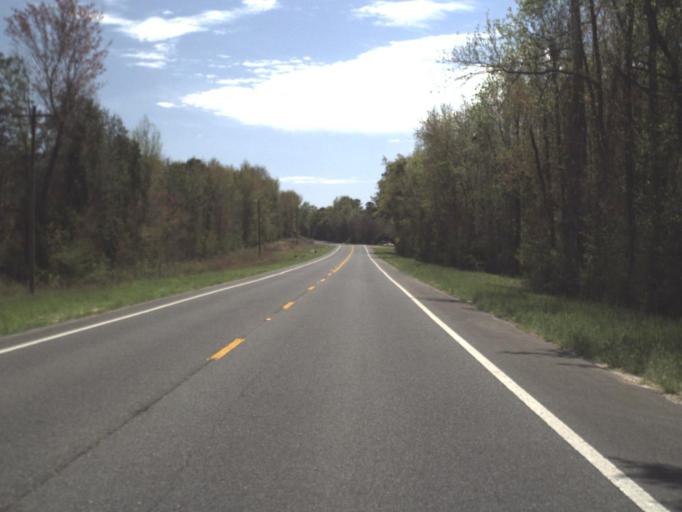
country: US
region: Alabama
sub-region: Geneva County
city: Geneva
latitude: 30.9716
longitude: -85.9980
